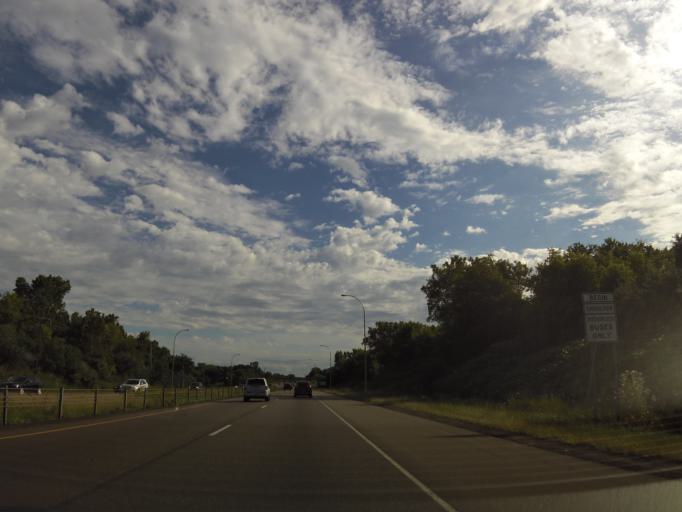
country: US
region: Minnesota
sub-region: Hennepin County
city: New Hope
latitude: 45.0748
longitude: -93.4018
